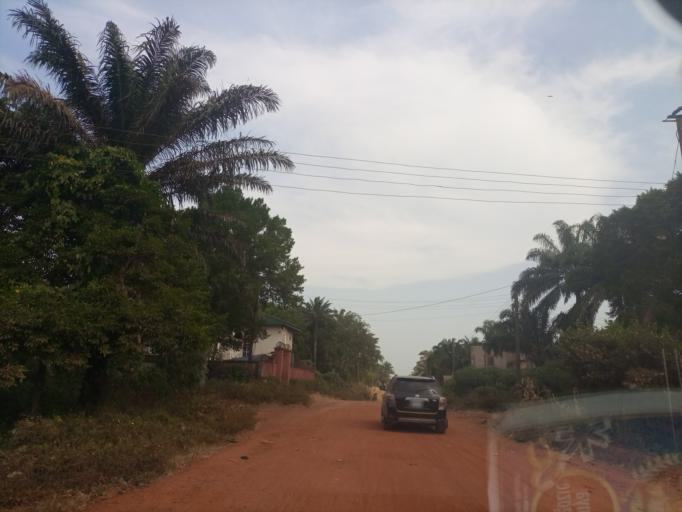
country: NG
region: Enugu
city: Opi
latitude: 6.8225
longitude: 7.4732
